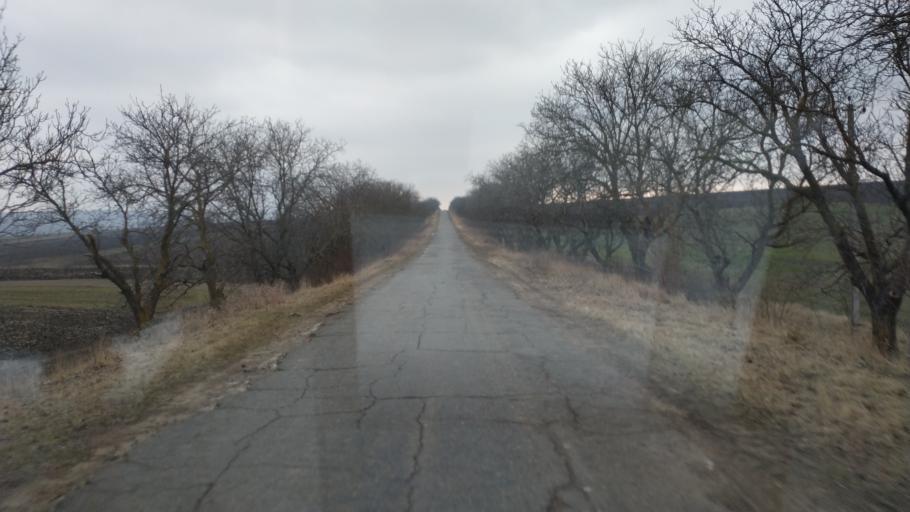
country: MD
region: Hincesti
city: Dancu
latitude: 46.8738
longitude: 28.2956
